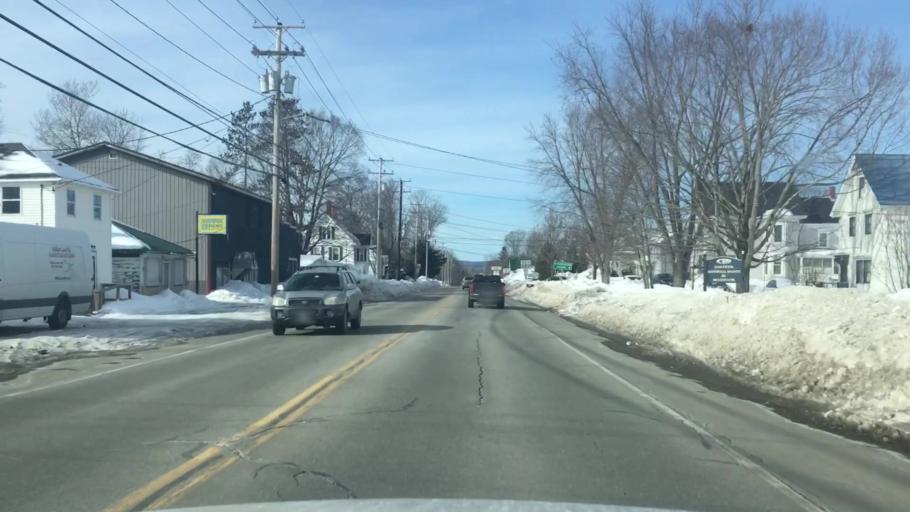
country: US
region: Maine
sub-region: Penobscot County
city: Charleston
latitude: 45.0037
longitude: -69.0234
